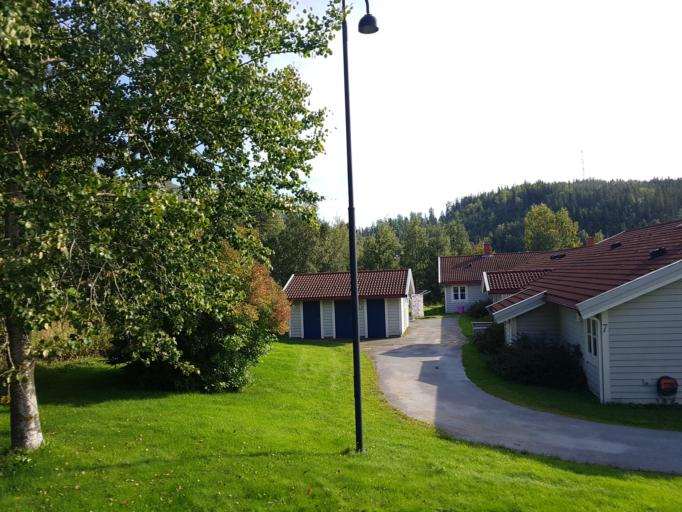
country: NO
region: Sor-Trondelag
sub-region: Afjord
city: A i Afjord
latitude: 63.9673
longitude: 10.2166
